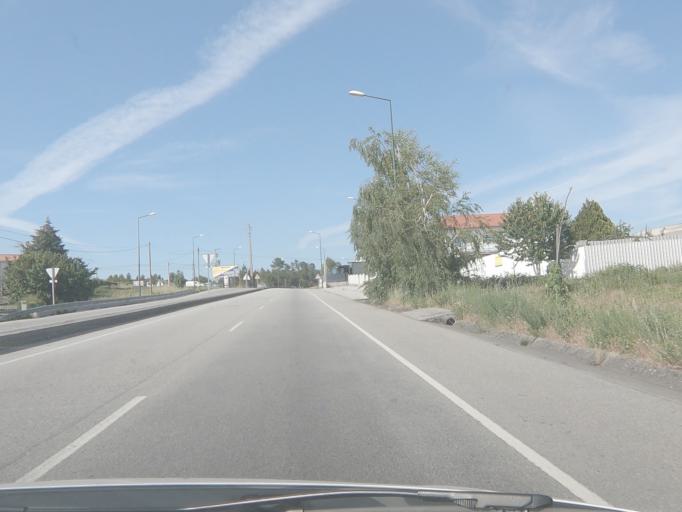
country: PT
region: Viseu
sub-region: Viseu
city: Viseu
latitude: 40.6259
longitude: -7.9425
